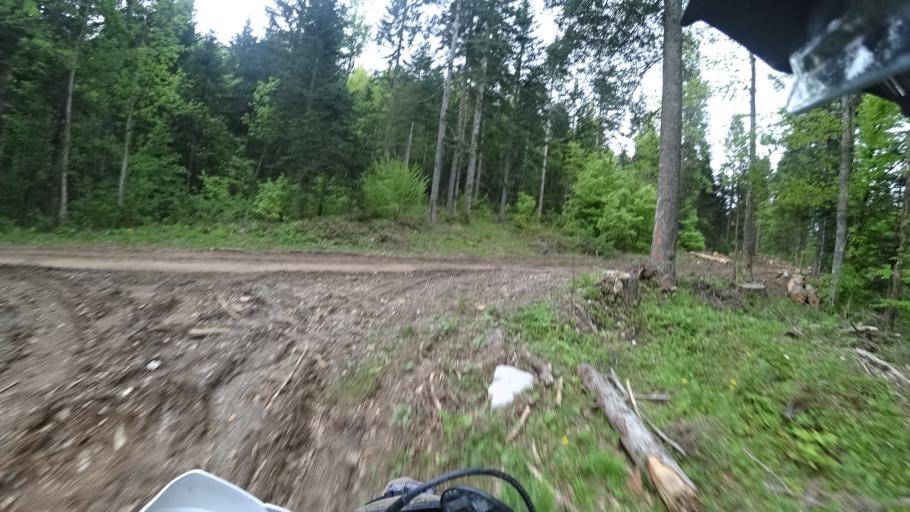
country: HR
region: Karlovacka
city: Plaski
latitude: 44.9527
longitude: 15.4151
